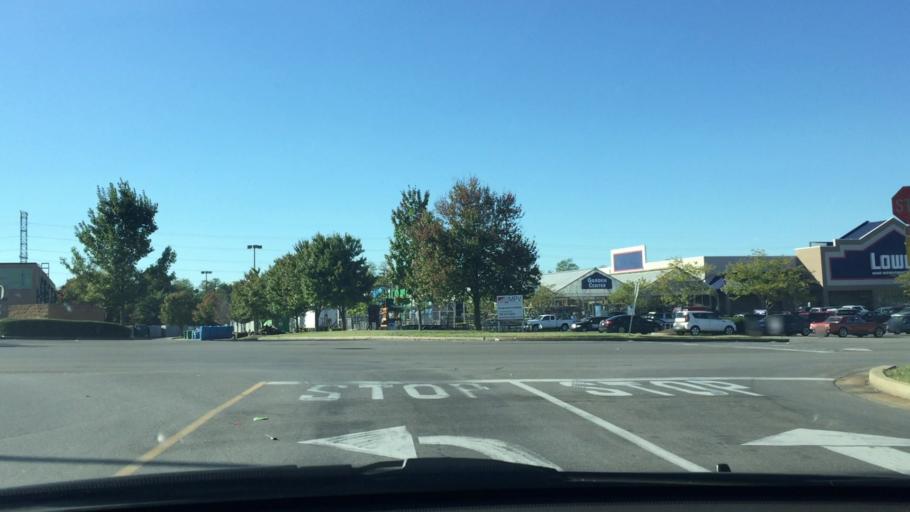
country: US
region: Kentucky
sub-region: Fayette County
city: Monticello
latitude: 37.9784
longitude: -84.5332
